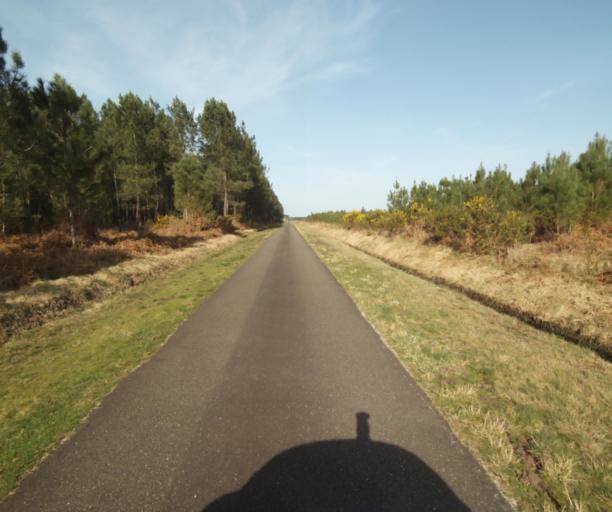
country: FR
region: Aquitaine
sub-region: Departement des Landes
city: Sarbazan
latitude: 44.1358
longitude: -0.1573
